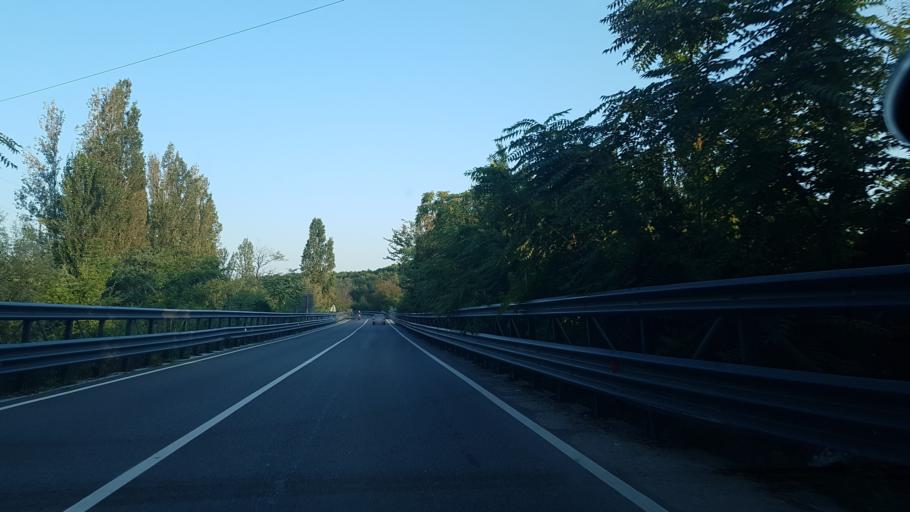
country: IT
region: Friuli Venezia Giulia
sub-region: Provincia di Trieste
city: Duino
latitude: 45.7953
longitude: 13.5829
